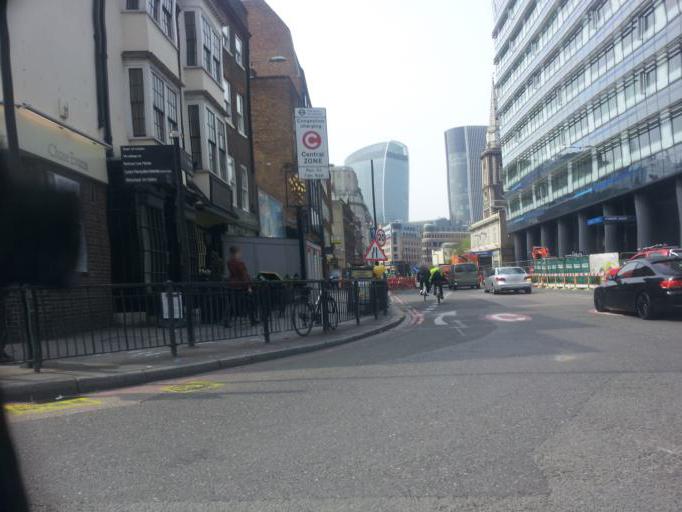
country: GB
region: England
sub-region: Greater London
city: Bethnal Green
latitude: 51.5146
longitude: -0.0738
